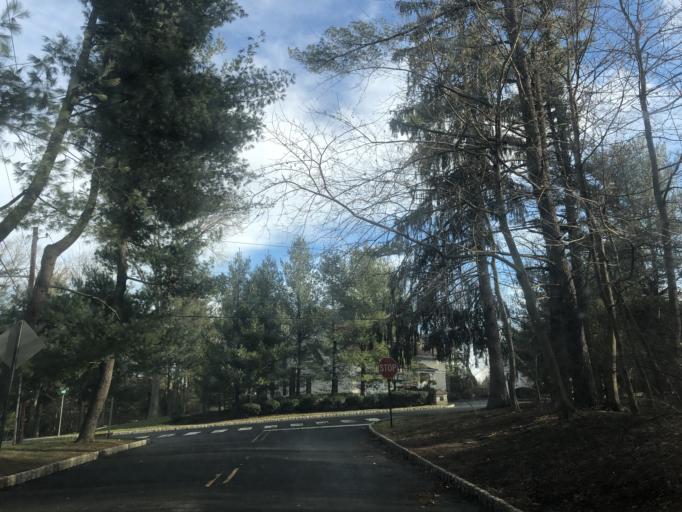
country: US
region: New Jersey
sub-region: Somerset County
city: Kingston
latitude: 40.3614
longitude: -74.6341
